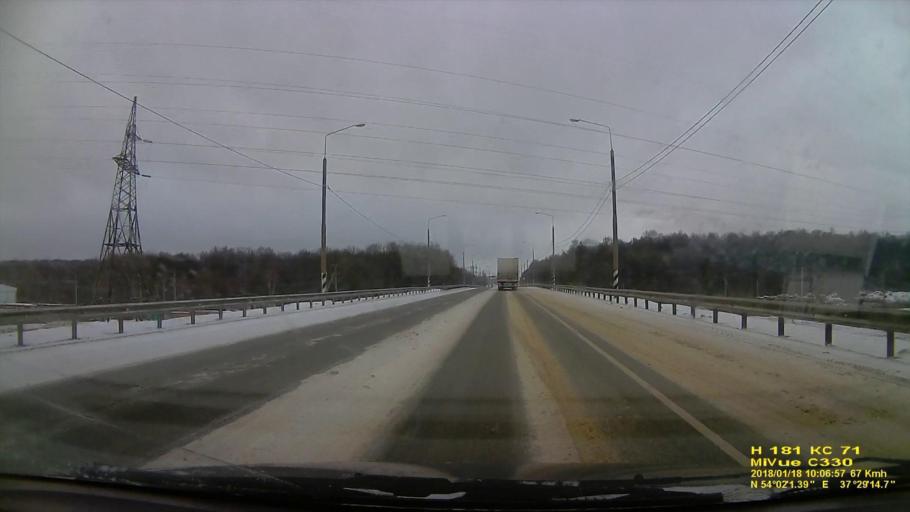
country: RU
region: Tula
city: Pervomayskiy
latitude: 54.0333
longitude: 37.4874
